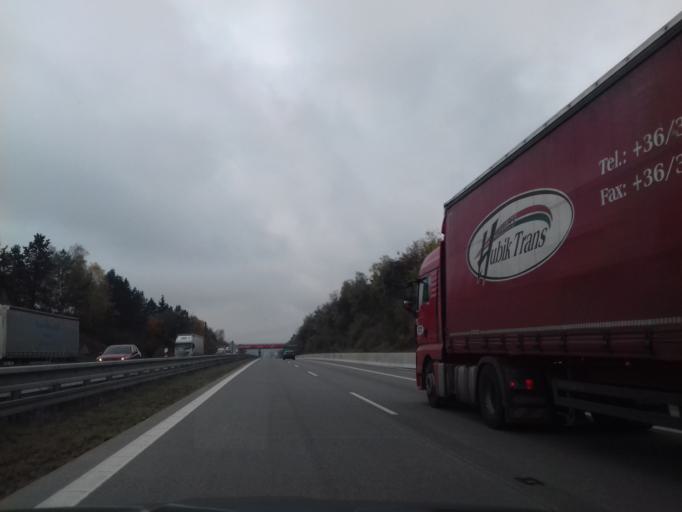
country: CZ
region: Central Bohemia
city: Cechtice
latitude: 49.6453
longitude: 15.1251
